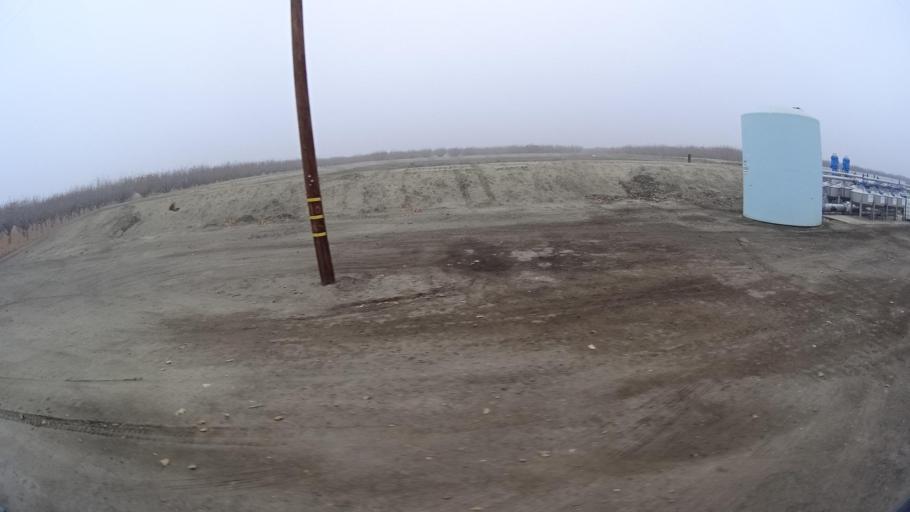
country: US
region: California
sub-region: Kern County
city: Buttonwillow
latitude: 35.4124
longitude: -119.5278
